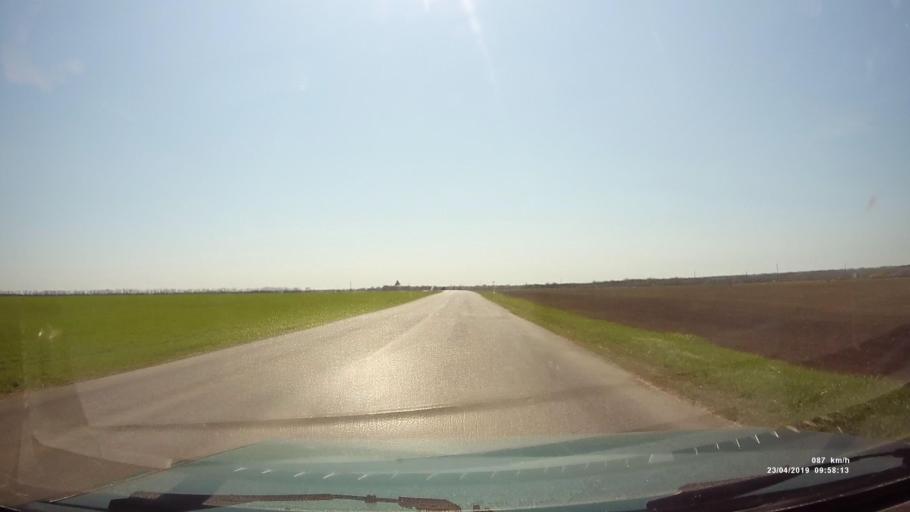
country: RU
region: Rostov
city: Sovetskoye
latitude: 46.7814
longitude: 42.0963
